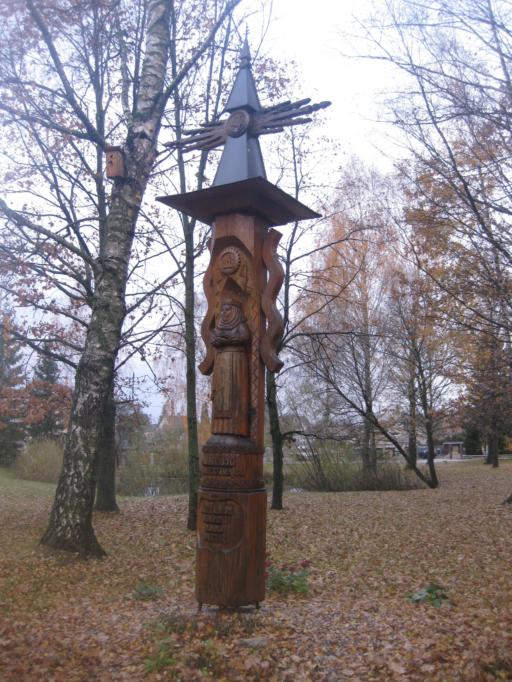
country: LT
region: Kauno apskritis
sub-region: Kaunas
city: Aleksotas
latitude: 54.8583
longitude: 23.8811
